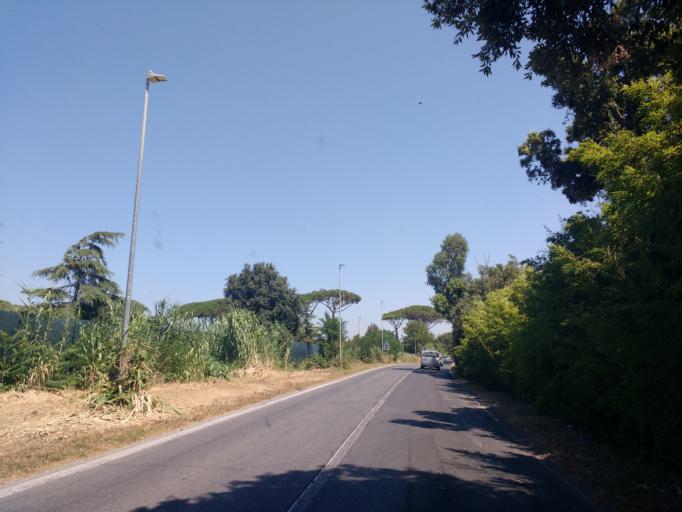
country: IT
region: Latium
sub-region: Citta metropolitana di Roma Capitale
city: Maccarese
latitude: 41.8712
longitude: 12.2087
